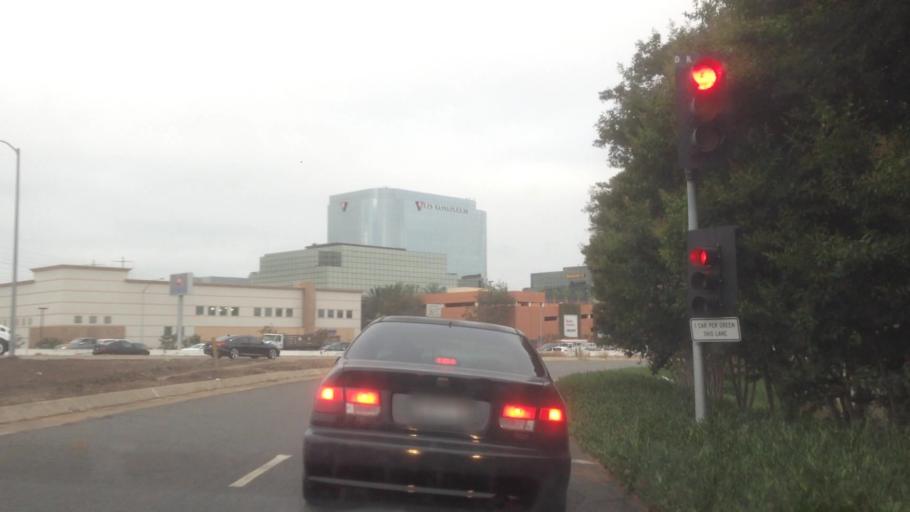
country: US
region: California
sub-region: Orange County
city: Midway City
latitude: 33.7350
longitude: -117.9913
